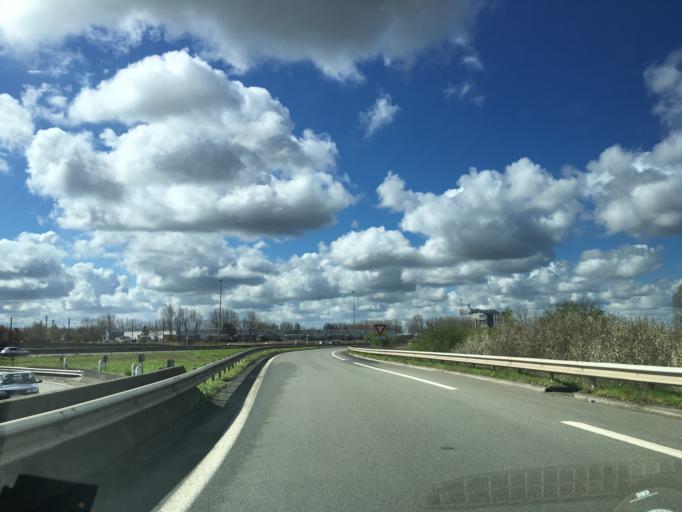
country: FR
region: Nord-Pas-de-Calais
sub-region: Departement du Nord
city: Grande-Synthe
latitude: 51.0081
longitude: 2.3227
